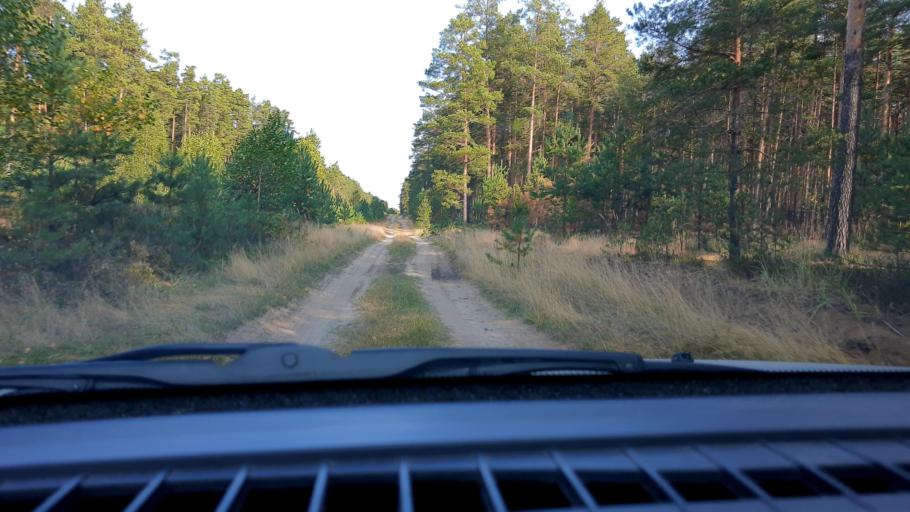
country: RU
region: Nizjnij Novgorod
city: Lukino
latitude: 56.4009
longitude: 43.6417
